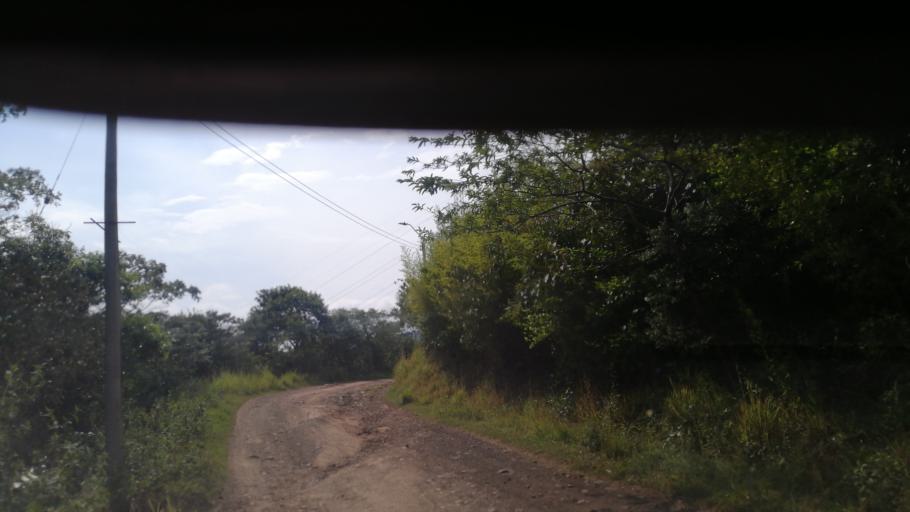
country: CO
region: Valle del Cauca
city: Cali
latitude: 3.4957
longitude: -76.5447
